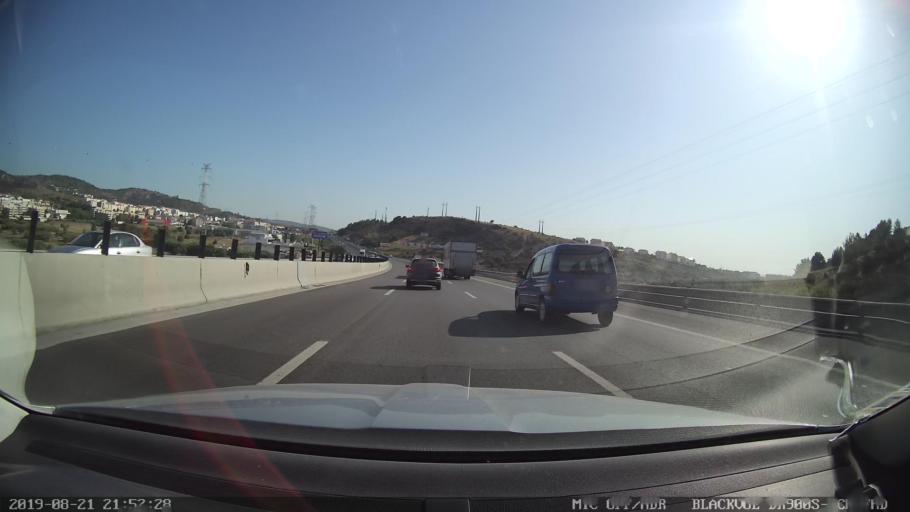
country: PT
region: Lisbon
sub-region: Vila Franca de Xira
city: Vialonga
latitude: 38.8693
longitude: -9.0705
